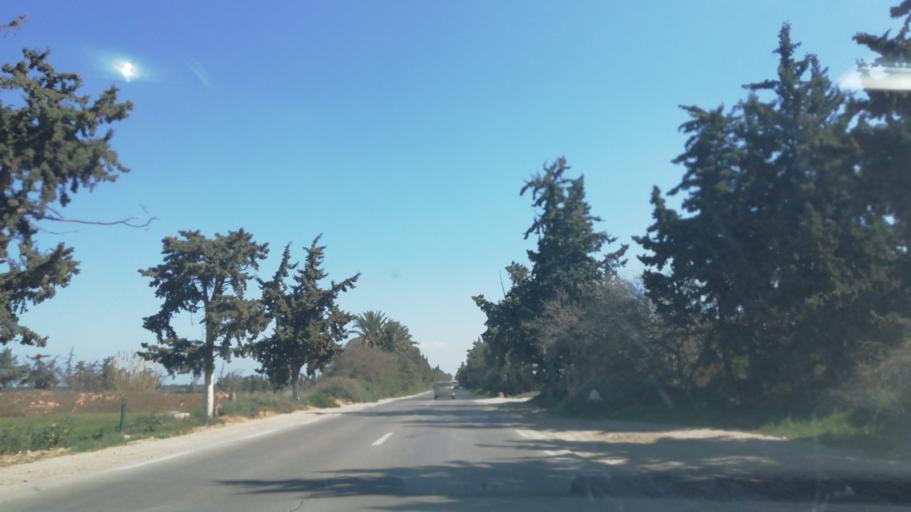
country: DZ
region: Mascara
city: Sig
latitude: 35.5734
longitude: -0.0163
